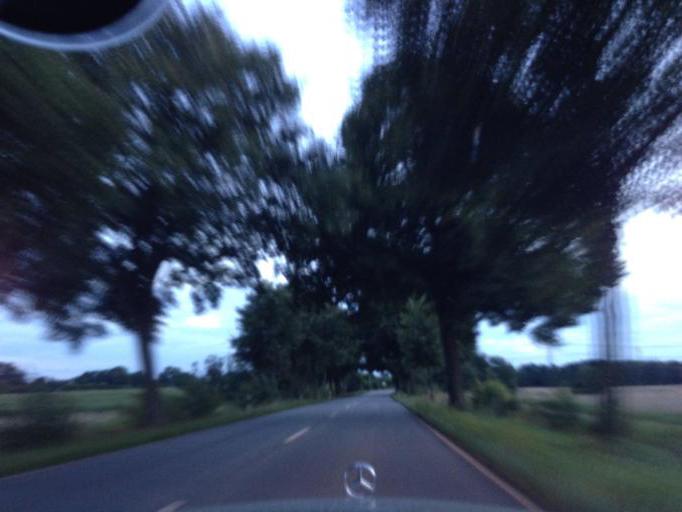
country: DE
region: Schleswig-Holstein
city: Stapelfeld
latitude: 53.6392
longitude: 10.1940
